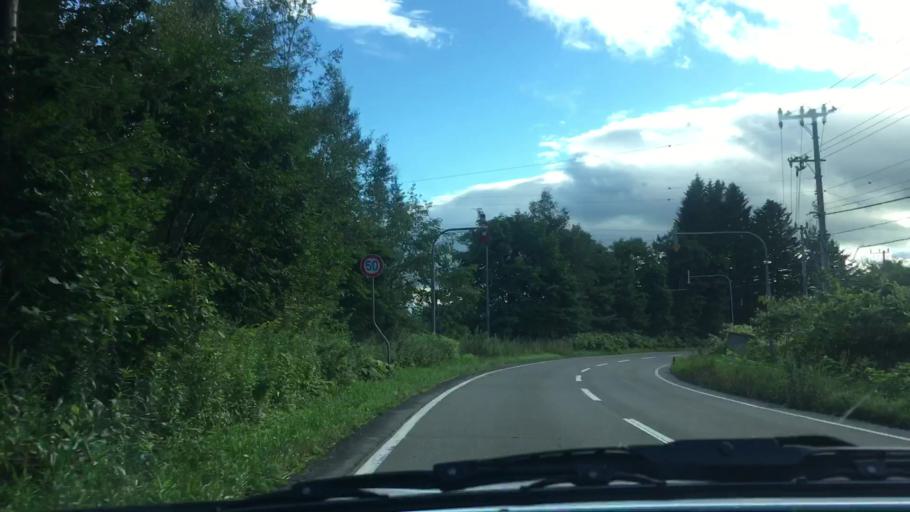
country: JP
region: Hokkaido
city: Otofuke
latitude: 43.1742
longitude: 142.9188
